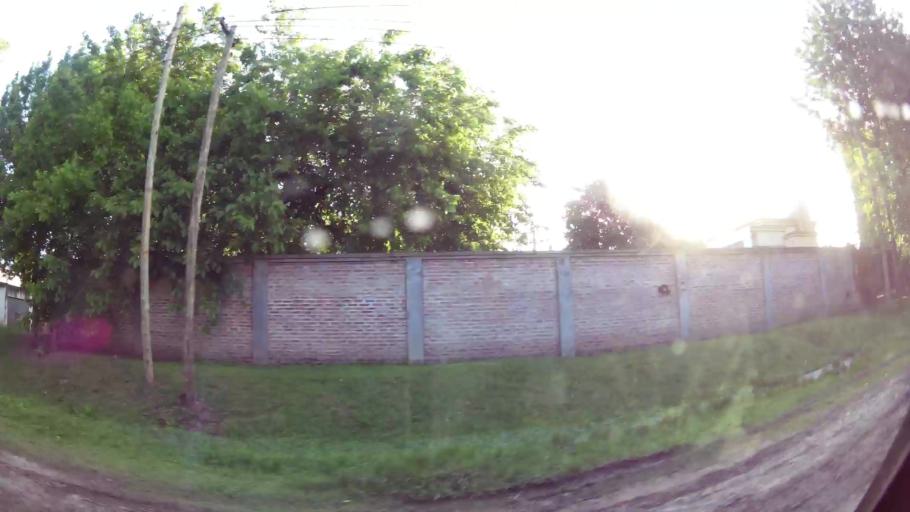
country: AR
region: Buenos Aires
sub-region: Partido de Quilmes
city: Quilmes
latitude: -34.8050
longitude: -58.2046
